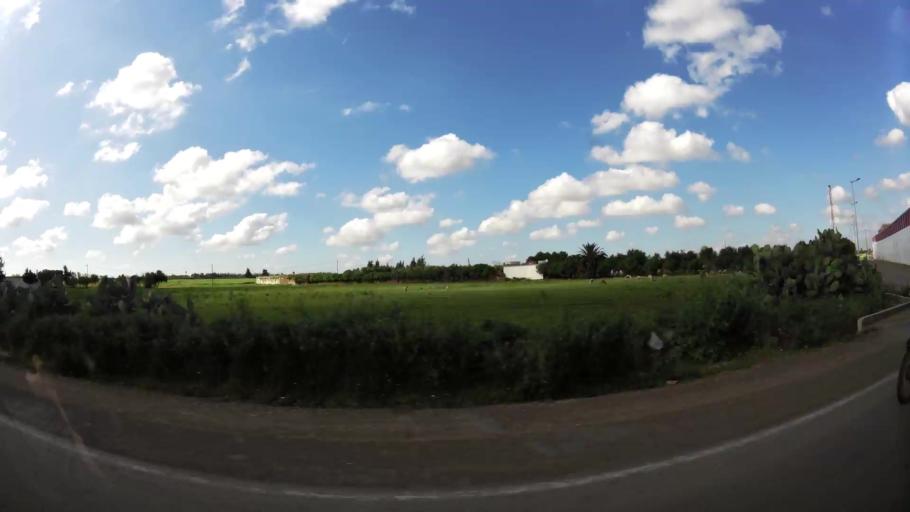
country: MA
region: Grand Casablanca
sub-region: Mediouna
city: Mediouna
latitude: 33.4075
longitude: -7.5465
